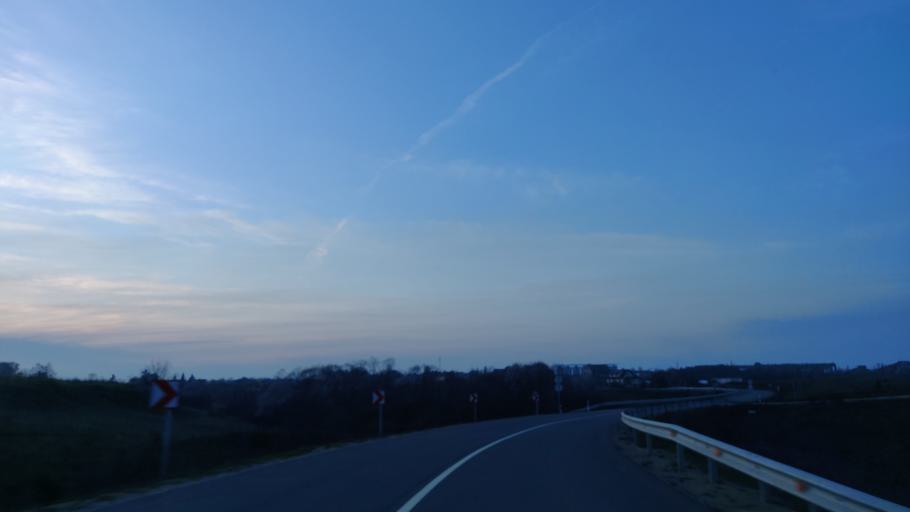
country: LT
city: Trakai
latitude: 54.6077
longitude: 24.9945
